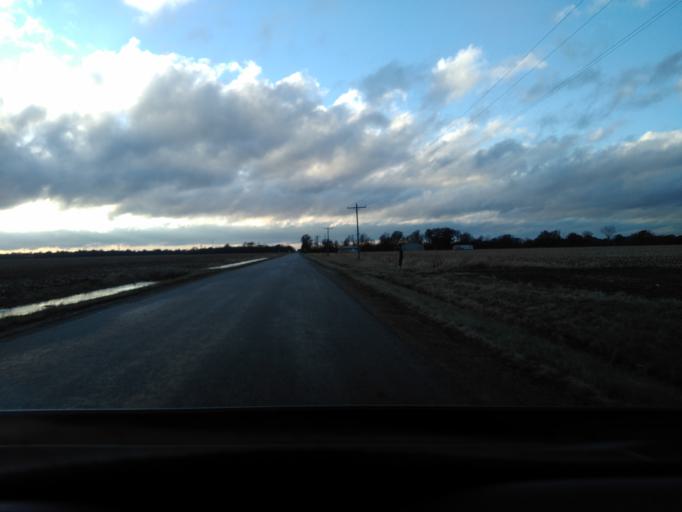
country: US
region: Illinois
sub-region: Effingham County
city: Altamont
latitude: 38.9573
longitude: -88.7439
